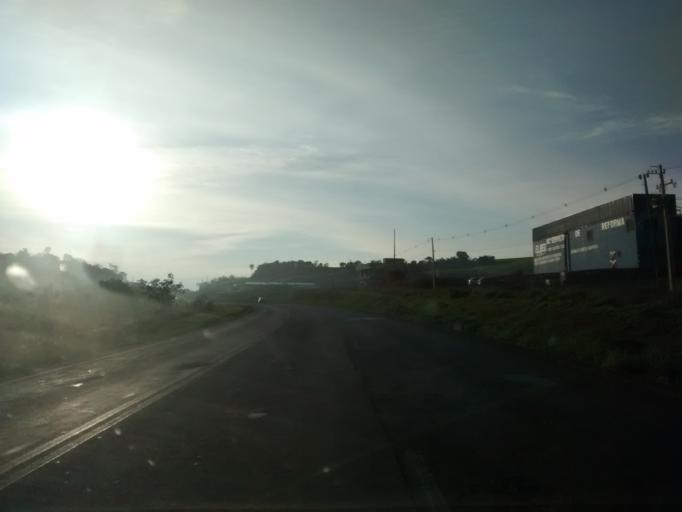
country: BR
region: Parana
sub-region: Francisco Beltrao
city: Francisco Beltrao
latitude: -26.1472
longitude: -53.0016
